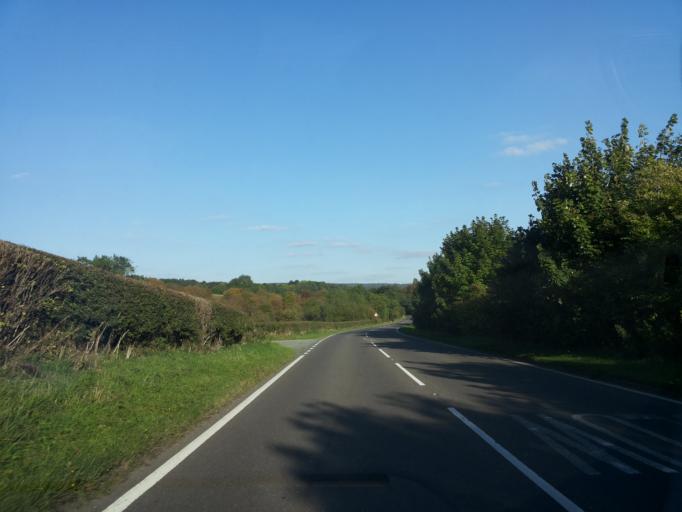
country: GB
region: England
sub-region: Derbyshire
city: Bakewell
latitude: 53.2386
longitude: -1.6511
